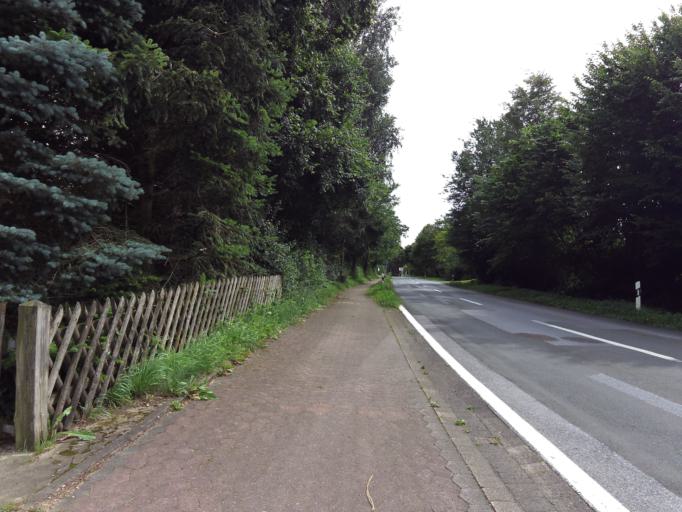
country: DE
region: North Rhine-Westphalia
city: Spenge
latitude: 52.1111
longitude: 8.4597
